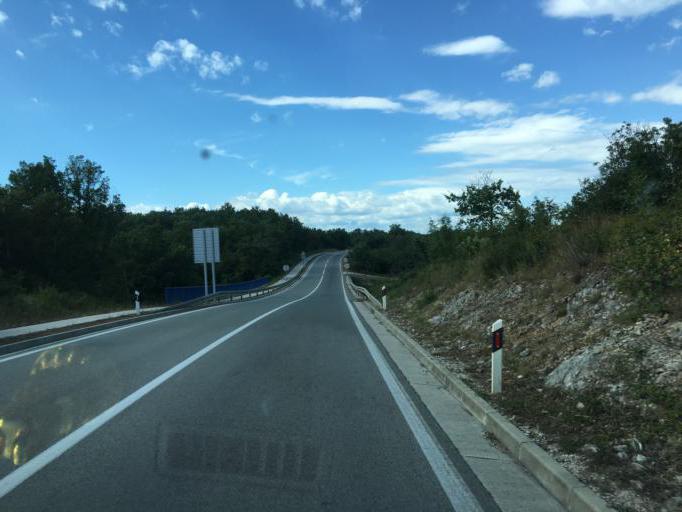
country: HR
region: Primorsko-Goranska
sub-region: Grad Krk
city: Krk
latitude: 45.0588
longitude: 14.5561
